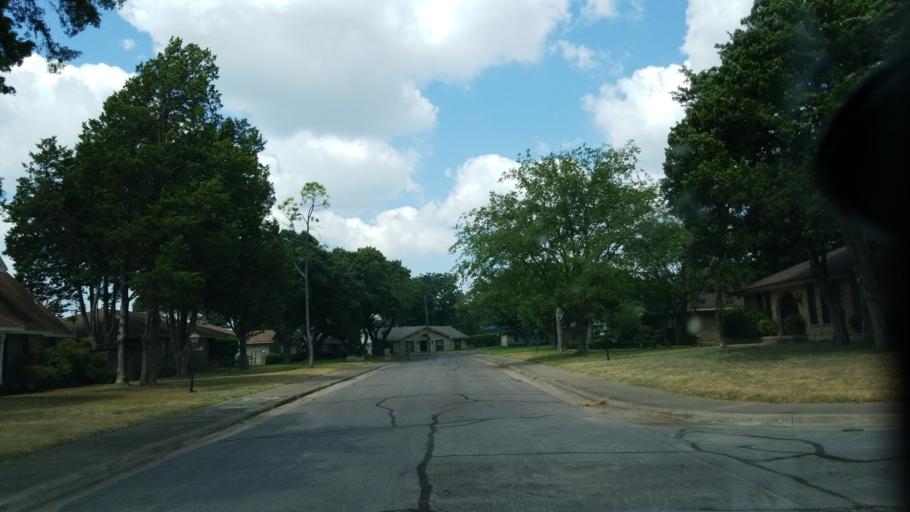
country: US
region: Texas
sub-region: Dallas County
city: Cockrell Hill
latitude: 32.6932
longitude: -96.8847
